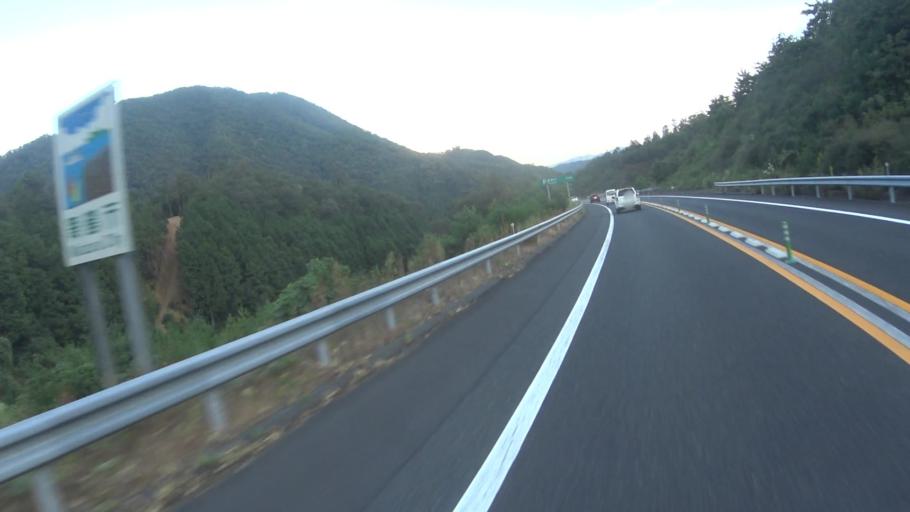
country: JP
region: Kyoto
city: Miyazu
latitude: 35.4529
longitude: 135.1795
